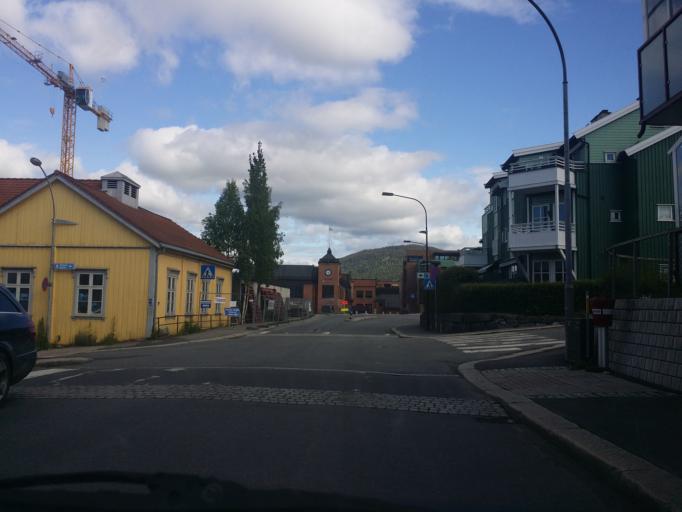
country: NO
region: Oppland
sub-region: Lillehammer
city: Lillehammer
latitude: 61.1154
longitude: 10.4688
